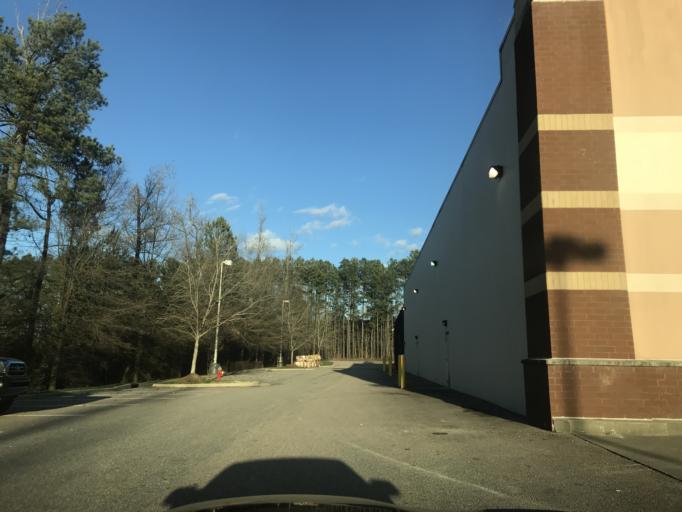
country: US
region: North Carolina
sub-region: Wake County
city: Knightdale
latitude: 35.7999
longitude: -78.5054
